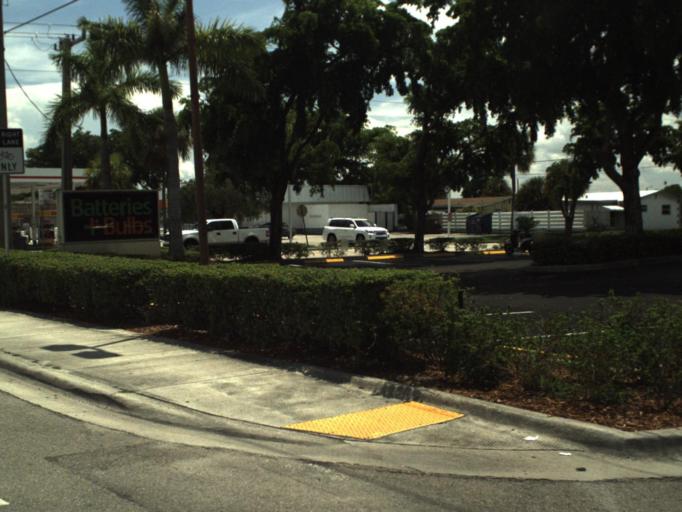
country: US
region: Florida
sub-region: Broward County
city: Plantation
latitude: 26.1571
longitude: -80.2574
